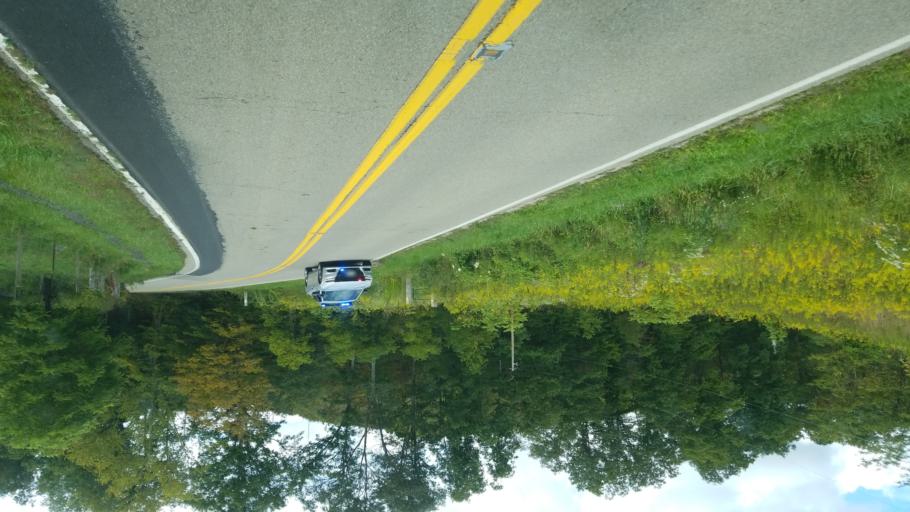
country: US
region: Ohio
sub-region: Jackson County
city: Oak Hill
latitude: 38.8862
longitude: -82.6813
